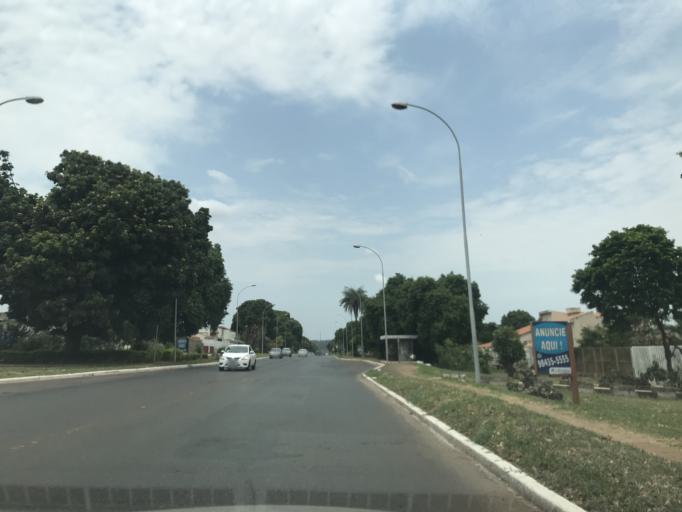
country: BR
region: Federal District
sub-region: Brasilia
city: Brasilia
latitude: -15.6531
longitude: -47.8044
